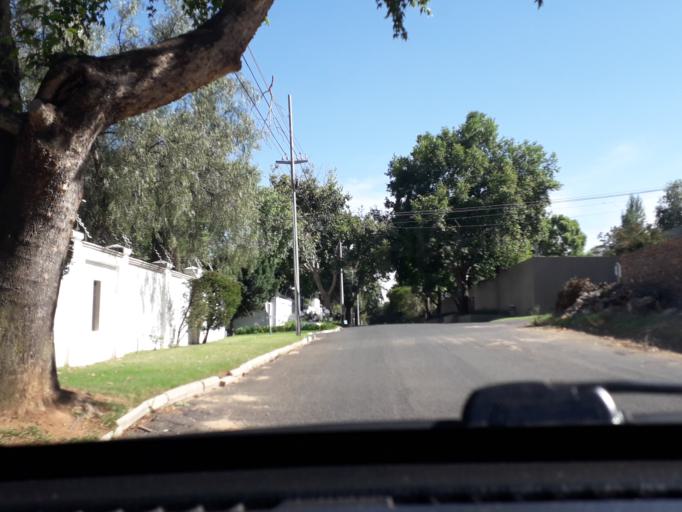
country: ZA
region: Gauteng
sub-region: City of Johannesburg Metropolitan Municipality
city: Johannesburg
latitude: -26.1358
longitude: 28.0224
